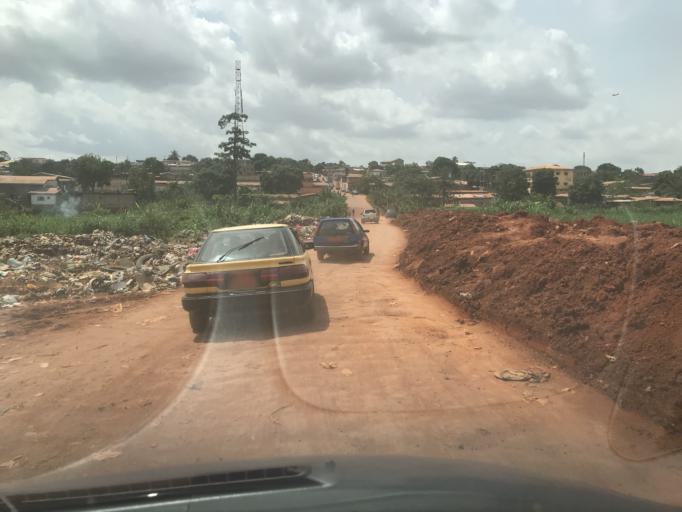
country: CM
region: Centre
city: Yaounde
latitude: 3.8465
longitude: 11.5323
